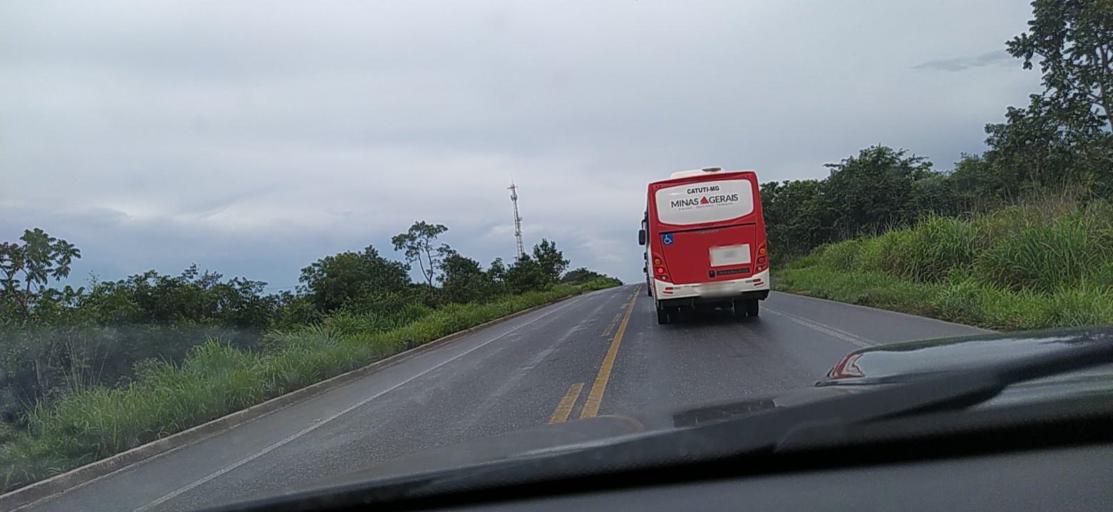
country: BR
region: Minas Gerais
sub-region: Montes Claros
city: Montes Claros
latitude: -16.6626
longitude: -43.7687
